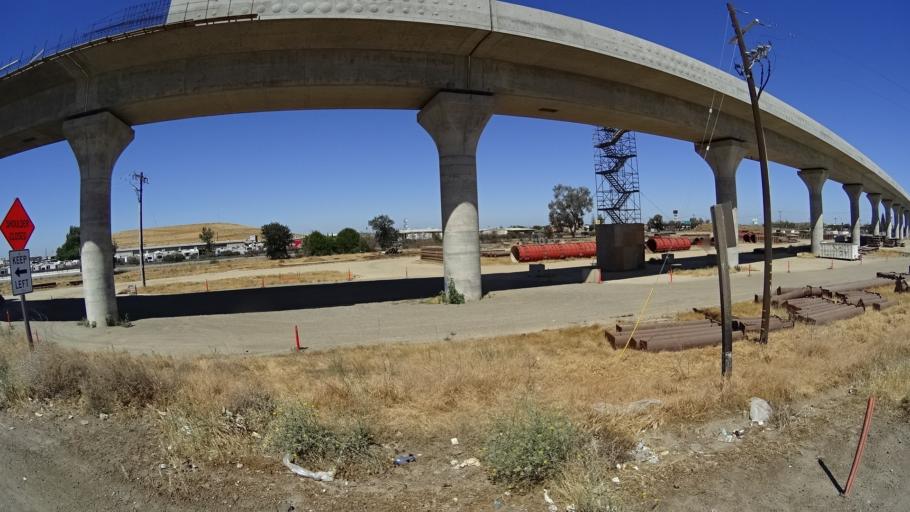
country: US
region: California
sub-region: Fresno County
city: Easton
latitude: 36.6907
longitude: -119.7544
